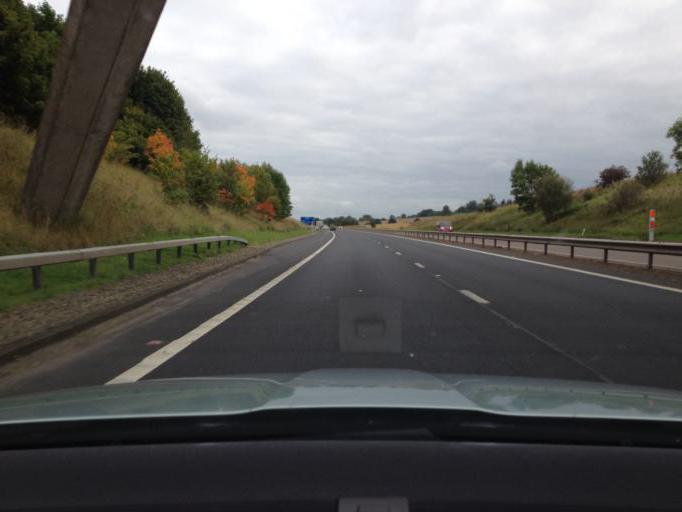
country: GB
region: Scotland
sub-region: Fife
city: Kelty
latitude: 56.1590
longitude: -3.4014
